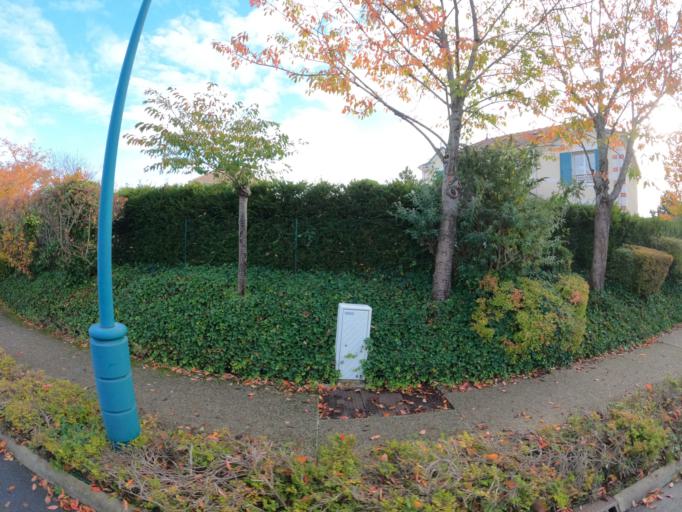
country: FR
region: Ile-de-France
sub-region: Departement de Seine-et-Marne
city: Magny-le-Hongre
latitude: 48.8687
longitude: 2.8211
